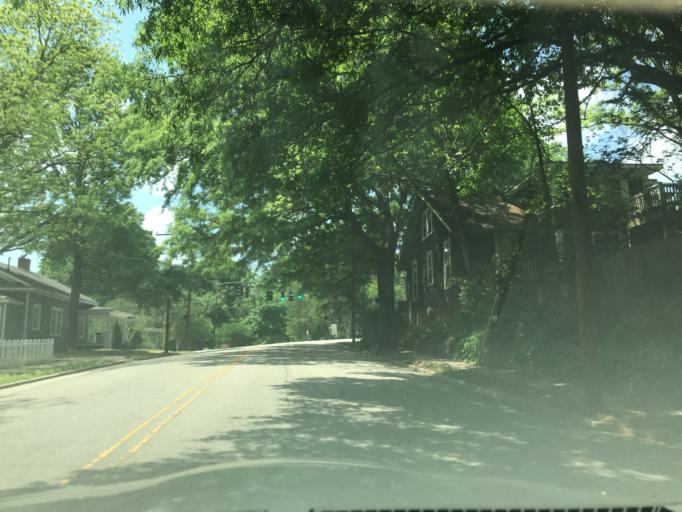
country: US
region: North Carolina
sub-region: Wake County
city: Raleigh
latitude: 35.7725
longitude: -78.6500
